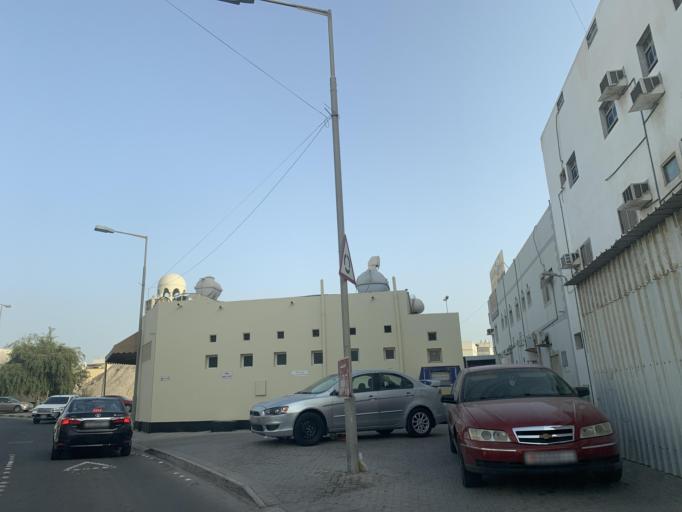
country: BH
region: Northern
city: Madinat `Isa
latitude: 26.1582
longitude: 50.5140
